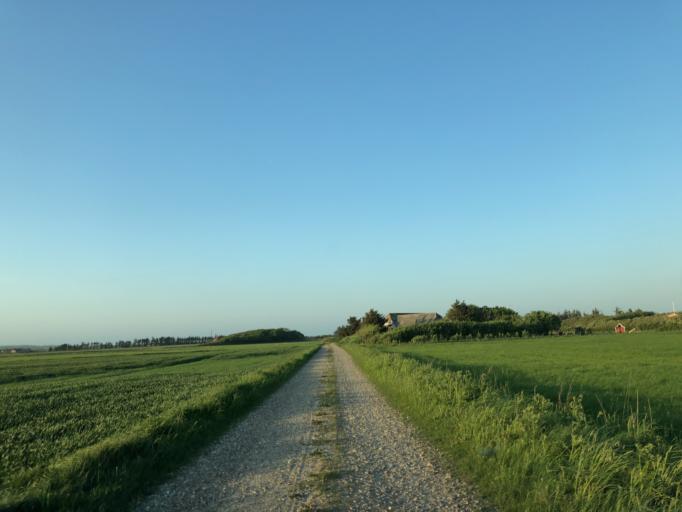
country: DK
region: Central Jutland
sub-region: Holstebro Kommune
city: Ulfborg
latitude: 56.2515
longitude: 8.1551
